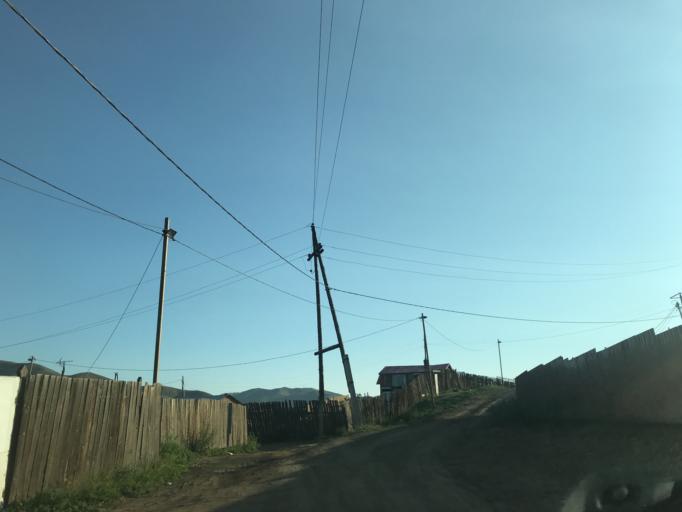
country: MN
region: Ulaanbaatar
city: Ulaanbaatar
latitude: 47.9903
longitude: 106.9647
